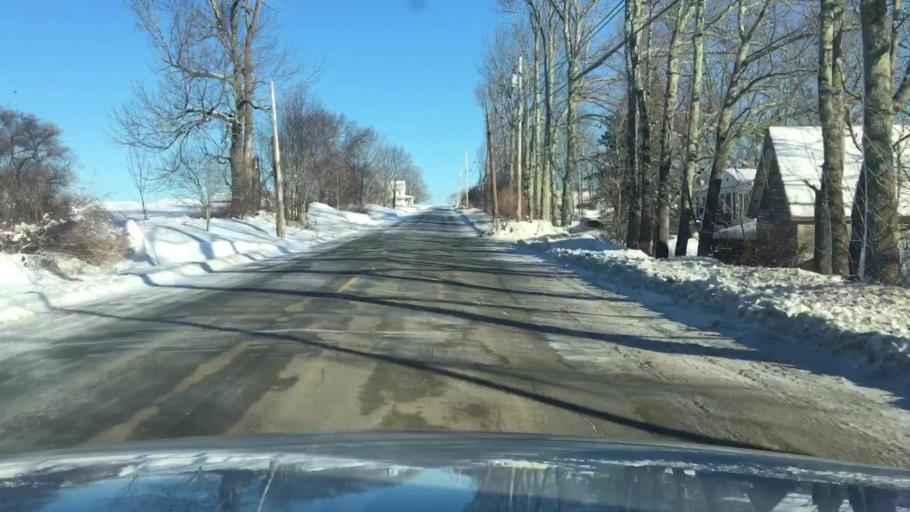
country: US
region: Maine
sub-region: Kennebec County
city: Mount Vernon
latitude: 44.4804
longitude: -69.9725
